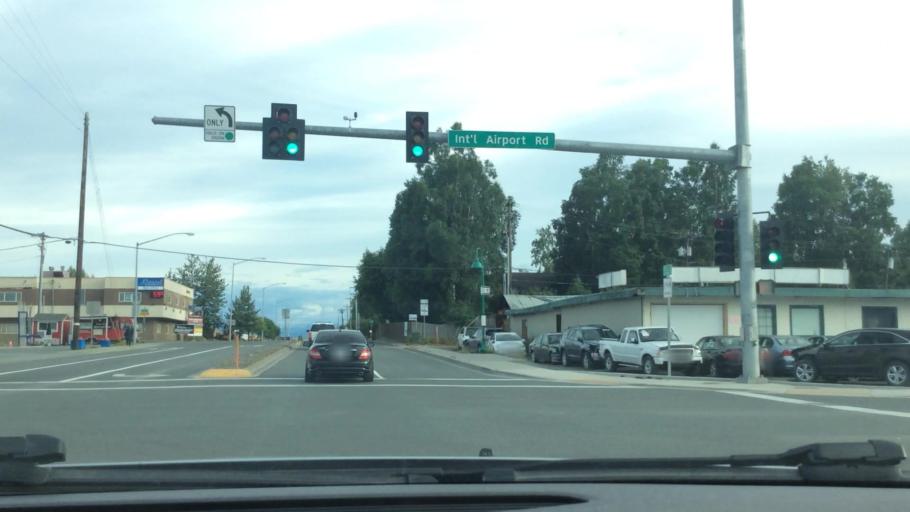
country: US
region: Alaska
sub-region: Anchorage Municipality
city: Anchorage
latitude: 61.1737
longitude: -149.8980
